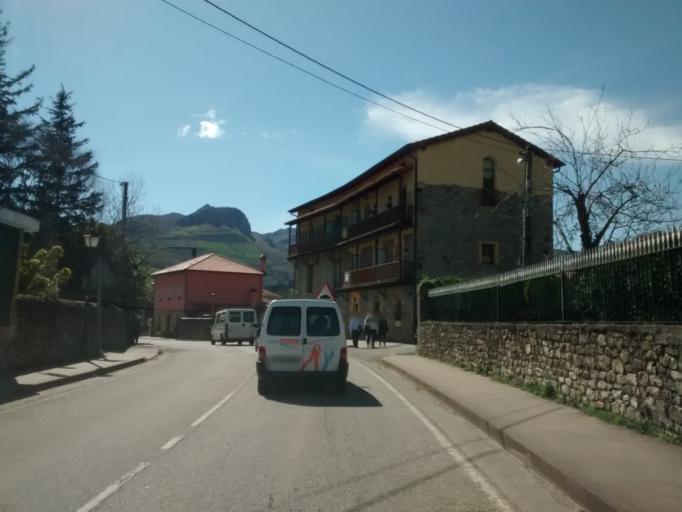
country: ES
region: Cantabria
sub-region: Provincia de Cantabria
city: Lierganes
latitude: 43.3398
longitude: -3.7445
